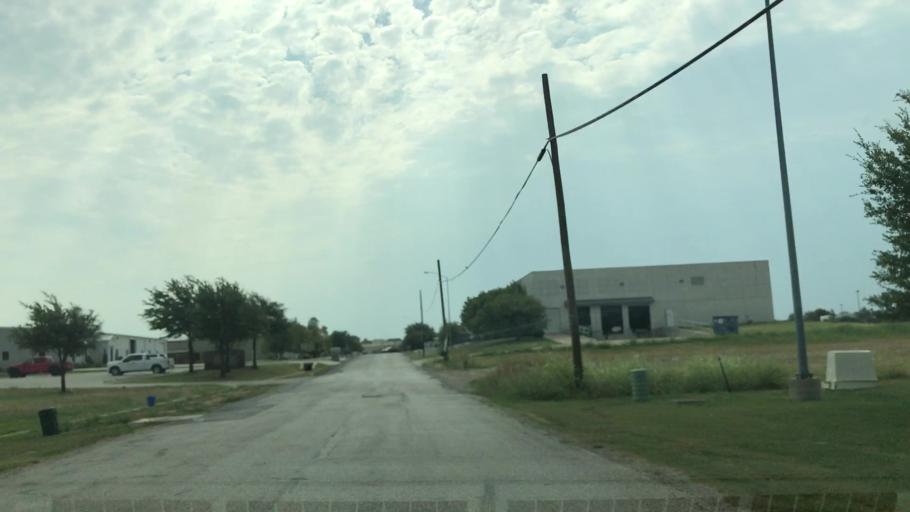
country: US
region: Texas
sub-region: Tarrant County
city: Keller
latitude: 32.9102
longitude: -97.2623
